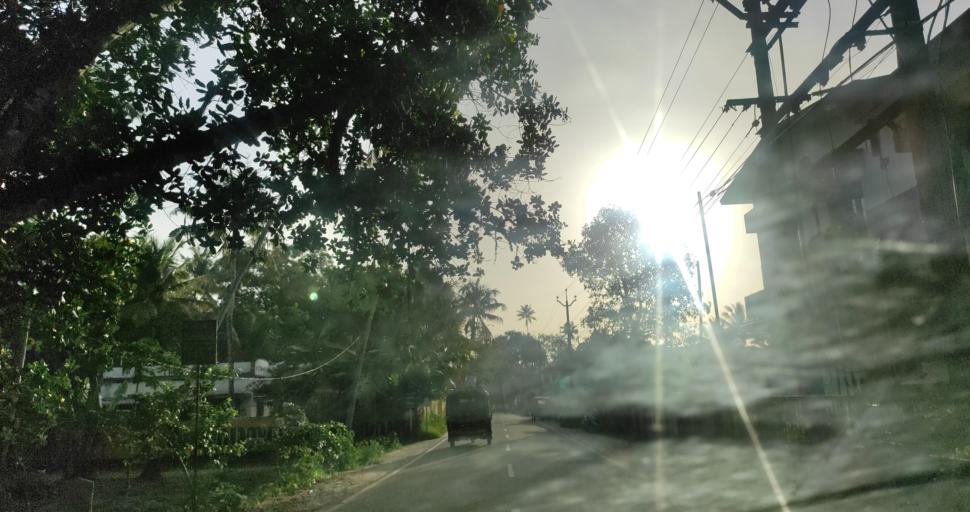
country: IN
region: Kerala
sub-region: Alappuzha
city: Shertallai
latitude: 9.6018
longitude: 76.3041
